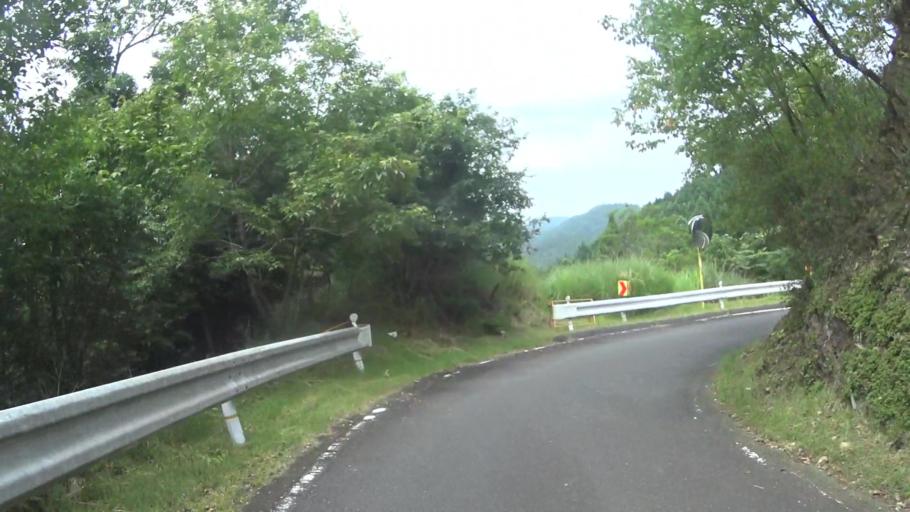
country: JP
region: Kyoto
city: Kameoka
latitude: 35.2028
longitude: 135.5828
